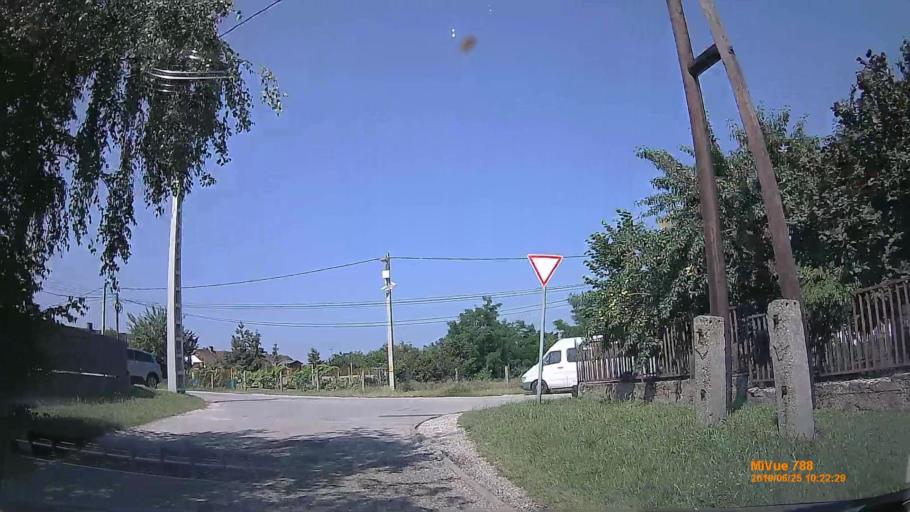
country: HU
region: Komarom-Esztergom
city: Tokod
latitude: 47.7338
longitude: 18.6936
